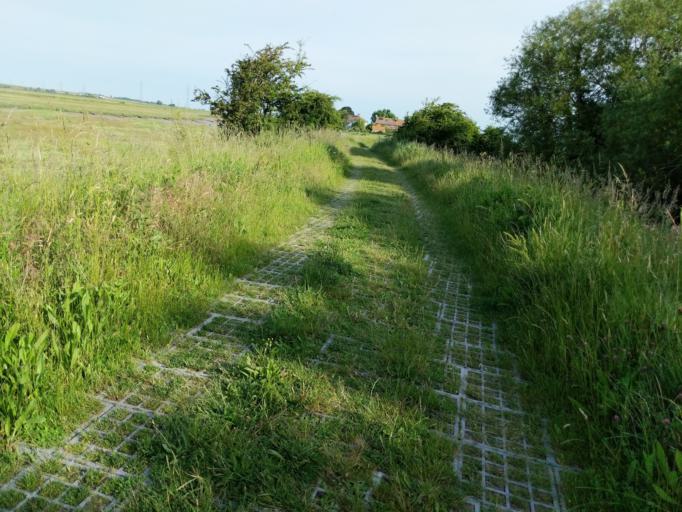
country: GB
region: England
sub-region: Kent
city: Faversham
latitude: 51.3288
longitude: 0.9176
